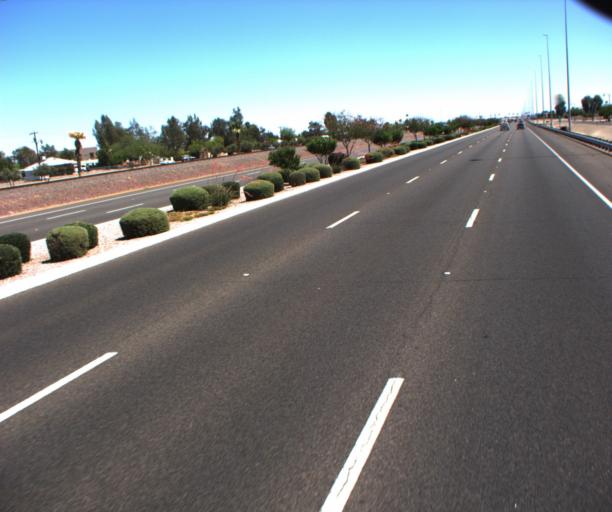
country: US
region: Arizona
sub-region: Maricopa County
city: Surprise
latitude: 33.6270
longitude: -112.3354
